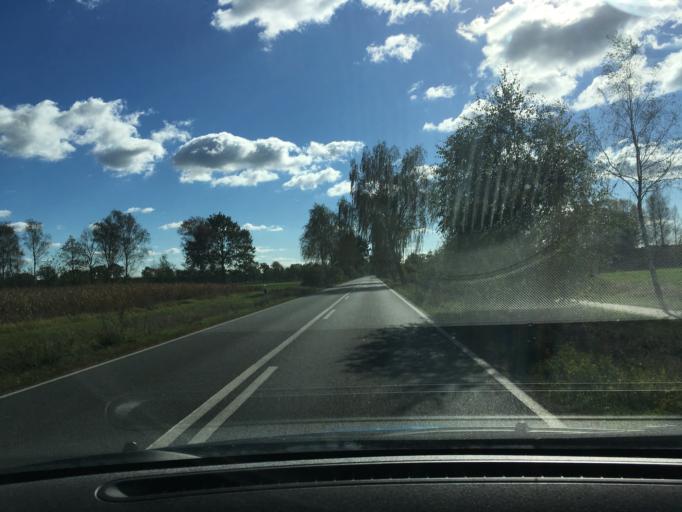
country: DE
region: Lower Saxony
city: Isernhagen Farster Bauerschaft
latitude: 52.5578
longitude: 9.8538
